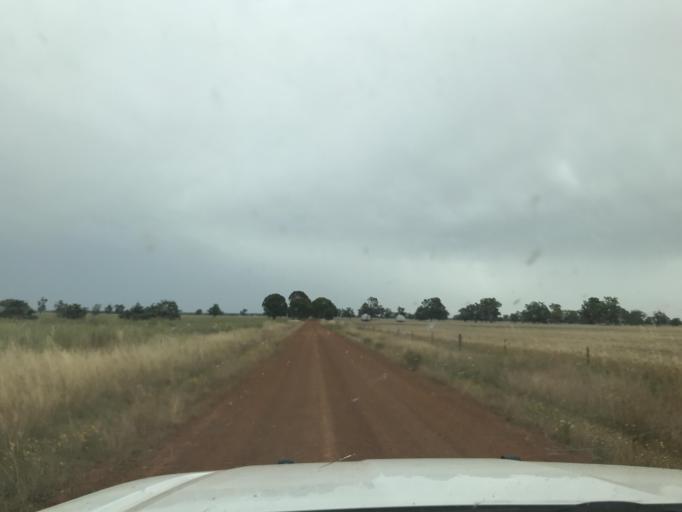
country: AU
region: Victoria
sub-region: Horsham
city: Horsham
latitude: -37.0628
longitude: 141.6348
